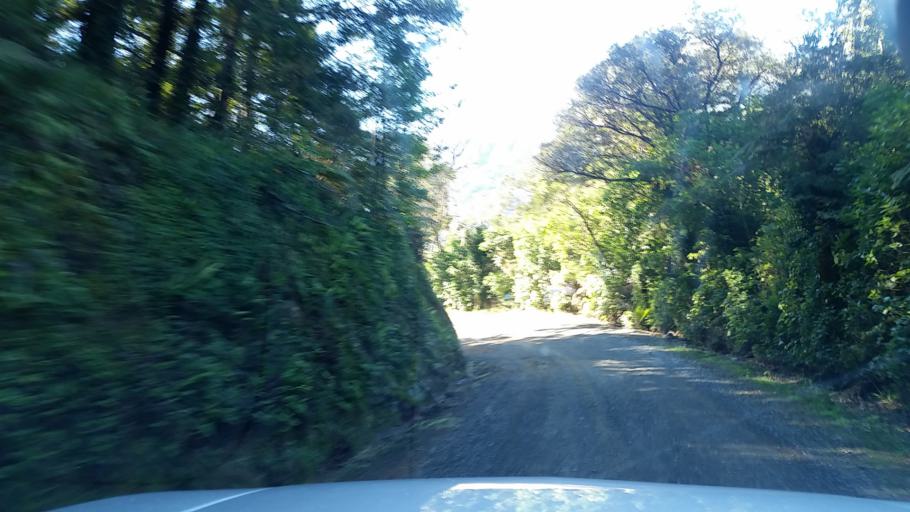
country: NZ
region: Marlborough
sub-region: Marlborough District
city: Picton
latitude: -41.1055
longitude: 173.6542
